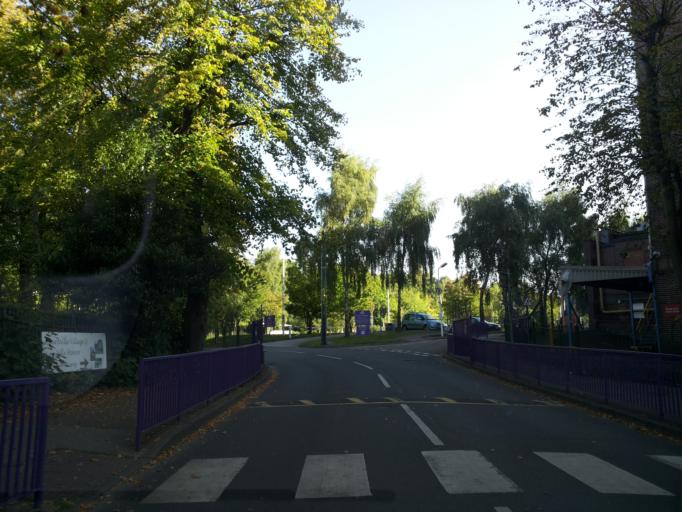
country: GB
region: England
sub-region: City and Borough of Birmingham
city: Birmingham
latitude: 52.4292
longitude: -1.9343
